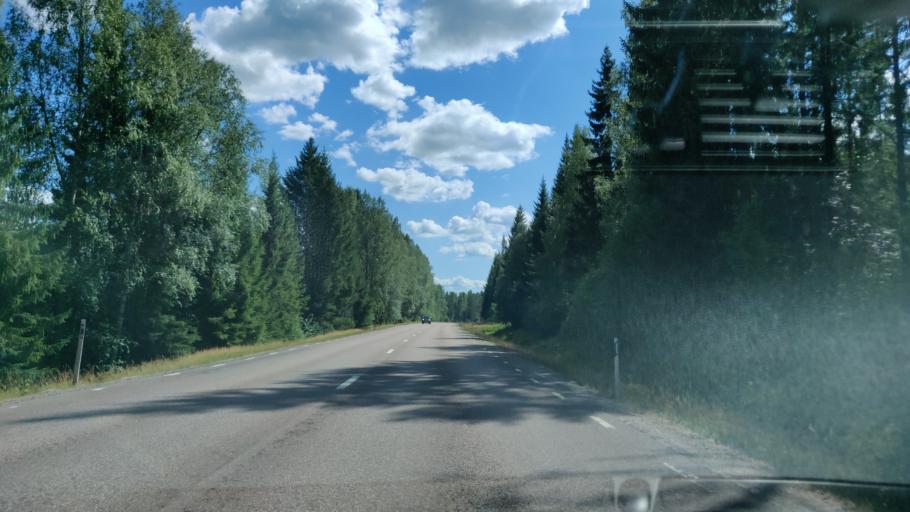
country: SE
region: Vaermland
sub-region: Hagfors Kommun
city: Ekshaerad
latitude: 60.1983
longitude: 13.4954
